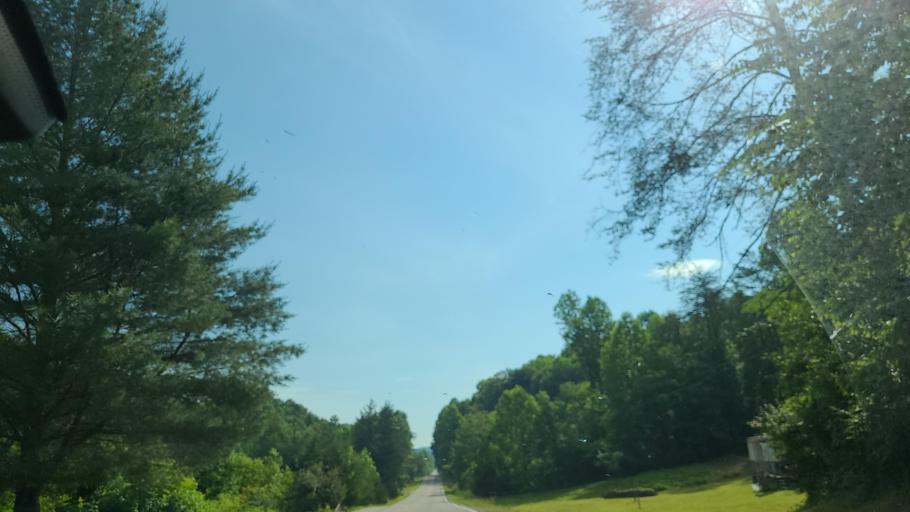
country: US
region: Kentucky
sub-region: Bell County
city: Middlesboro
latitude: 36.6944
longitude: -83.8628
